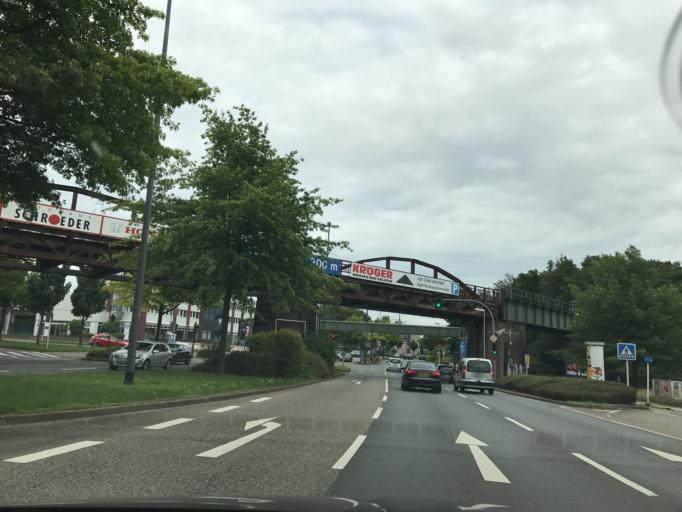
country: DE
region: North Rhine-Westphalia
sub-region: Regierungsbezirk Dusseldorf
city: Essen
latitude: 51.4734
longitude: 6.9881
